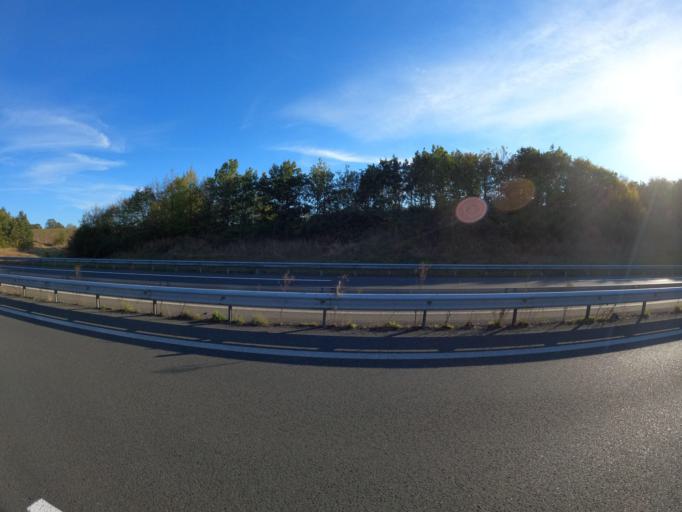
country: FR
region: Pays de la Loire
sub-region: Departement de Maine-et-Loire
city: Chemille-Melay
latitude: 47.2436
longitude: -0.6696
